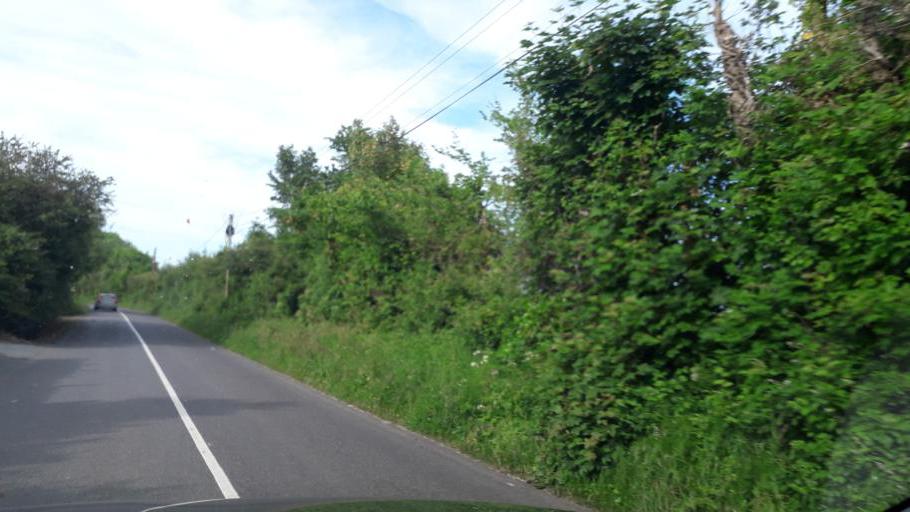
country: IE
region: Leinster
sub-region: Loch Garman
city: Courtown
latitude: 52.5605
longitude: -6.2331
